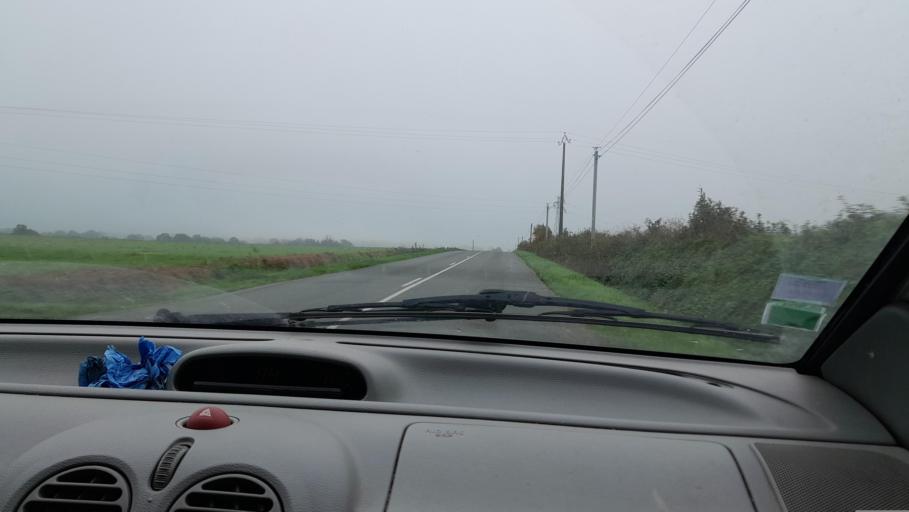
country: FR
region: Pays de la Loire
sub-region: Departement de la Mayenne
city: Loiron
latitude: 48.0259
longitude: -0.9187
